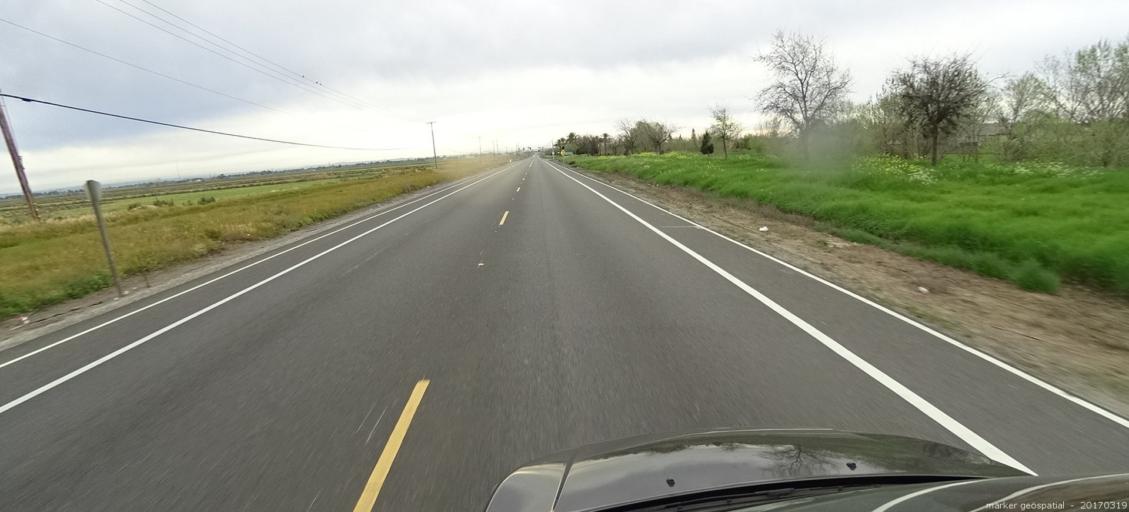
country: US
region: California
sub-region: Sacramento County
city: Elverta
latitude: 38.6852
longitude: -121.5199
